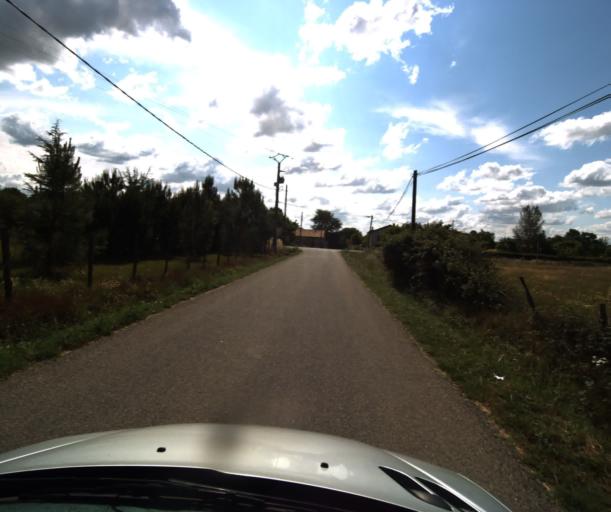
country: FR
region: Midi-Pyrenees
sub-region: Departement du Tarn-et-Garonne
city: Campsas
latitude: 43.8956
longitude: 1.3053
